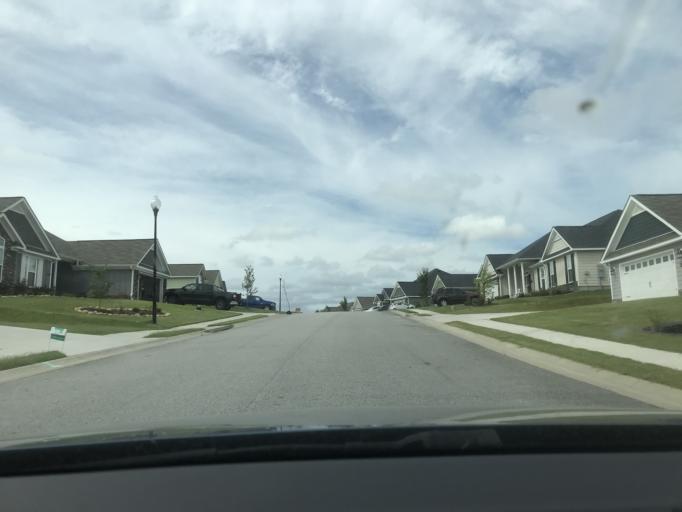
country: US
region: Georgia
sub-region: Columbia County
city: Grovetown
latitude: 33.4448
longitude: -82.1510
